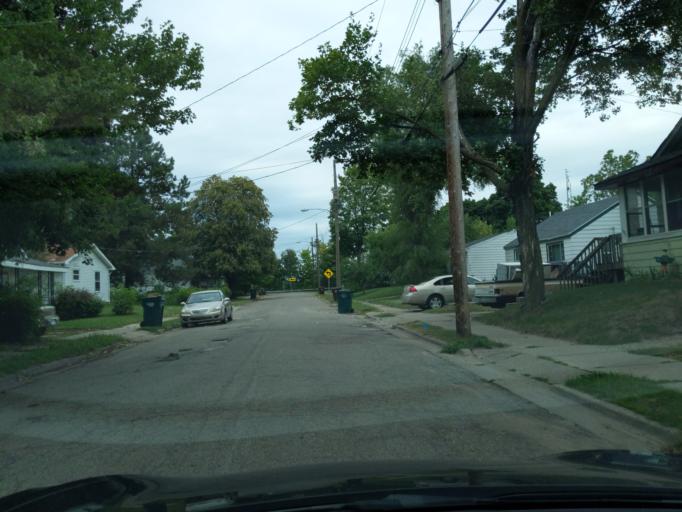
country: US
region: Michigan
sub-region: Ingham County
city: Lansing
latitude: 42.7231
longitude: -84.5286
